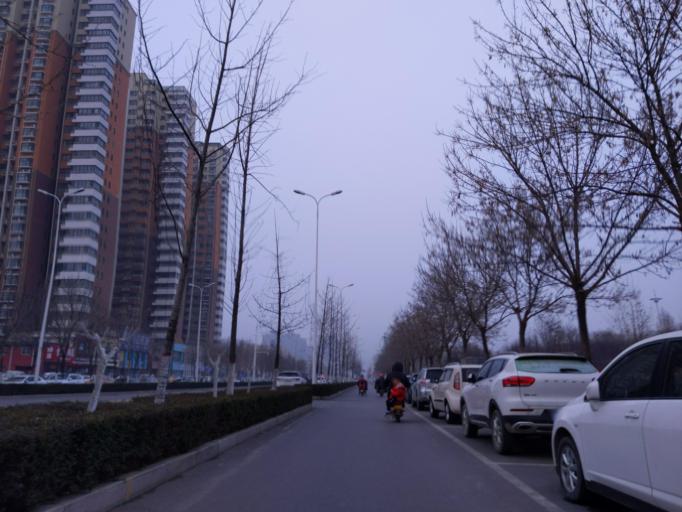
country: CN
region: Henan Sheng
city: Puyang
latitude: 35.7786
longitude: 115.0264
